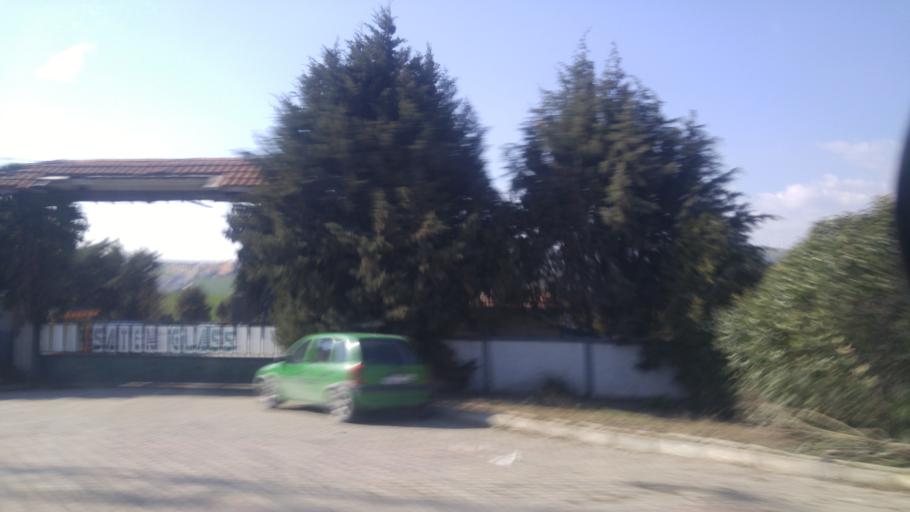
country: TR
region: Istanbul
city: Canta
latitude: 41.0968
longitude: 28.1101
